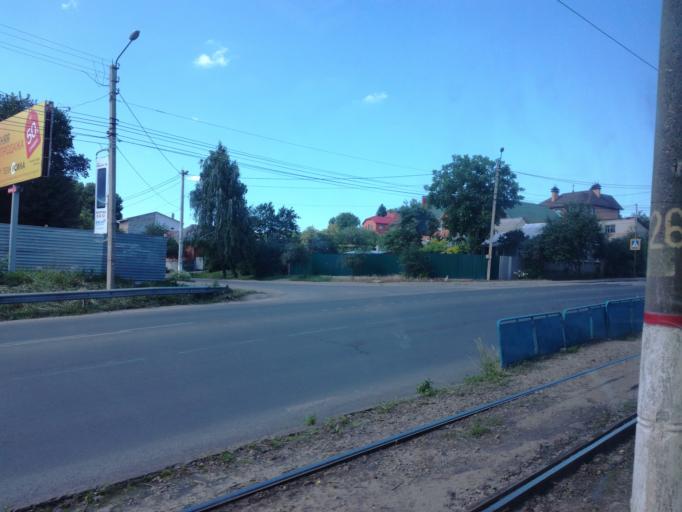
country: RU
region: Kursk
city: Kursk
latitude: 51.7502
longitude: 36.1743
